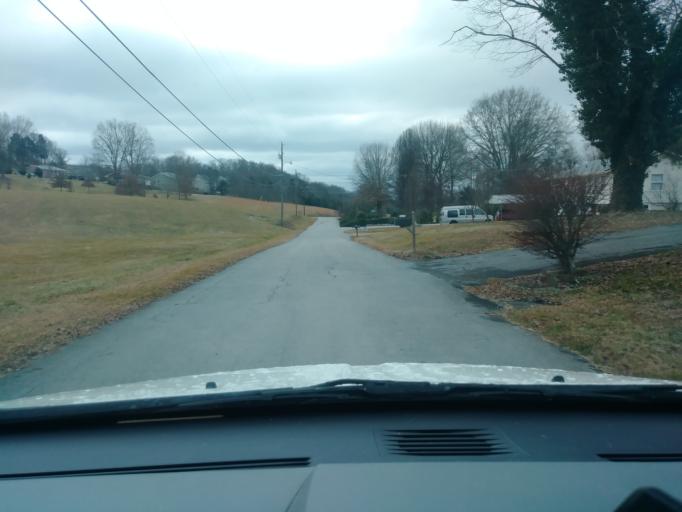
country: US
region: Tennessee
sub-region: Greene County
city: Greeneville
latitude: 36.1379
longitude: -82.8532
